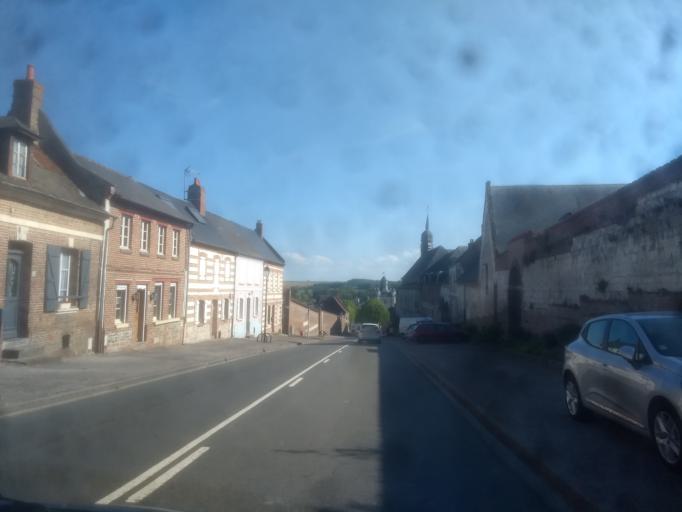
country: FR
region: Picardie
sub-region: Departement de la Somme
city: Saint-Riquier
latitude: 50.1365
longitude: 1.9459
